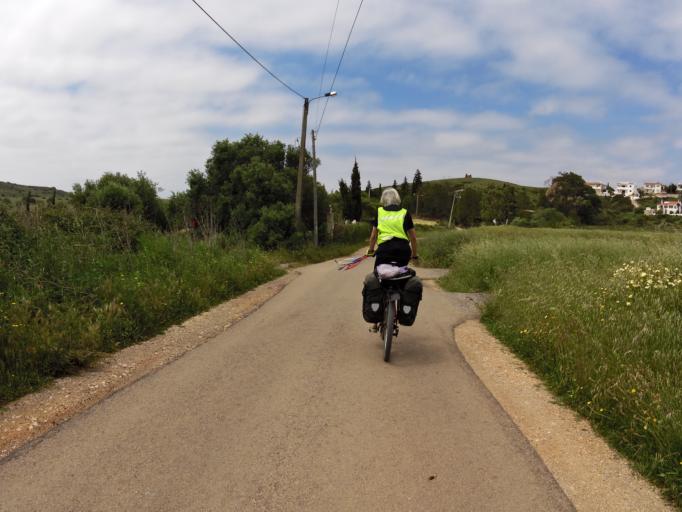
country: PT
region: Faro
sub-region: Vila do Bispo
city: Vila do Bispo
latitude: 37.0722
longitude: -8.8489
